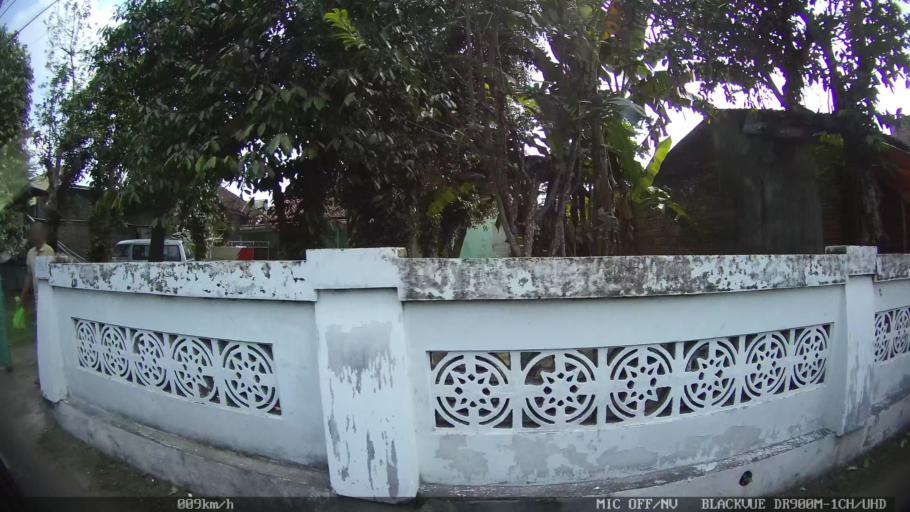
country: ID
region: Daerah Istimewa Yogyakarta
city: Yogyakarta
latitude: -7.8120
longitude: 110.3783
